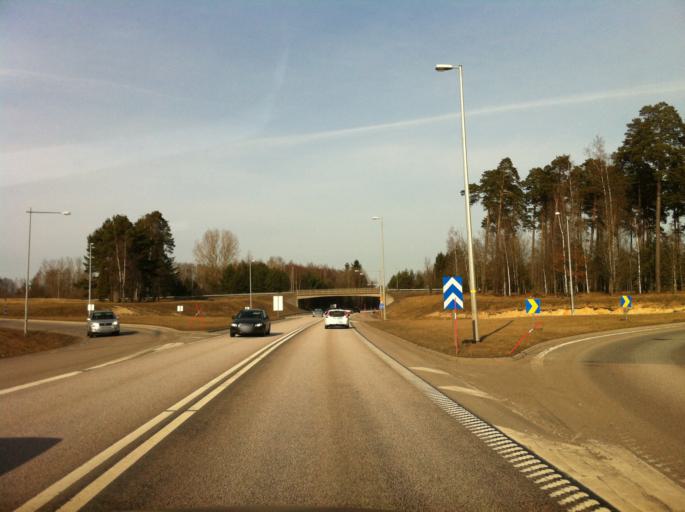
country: SE
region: Vaestra Goetaland
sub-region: Skovde Kommun
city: Skoevde
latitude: 58.3992
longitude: 13.8719
